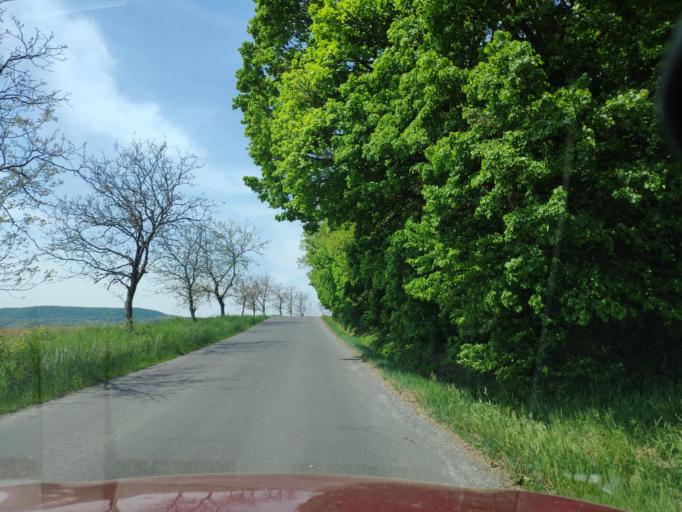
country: SK
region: Banskobystricky
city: Rimavska Sobota
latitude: 48.4673
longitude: 20.0911
